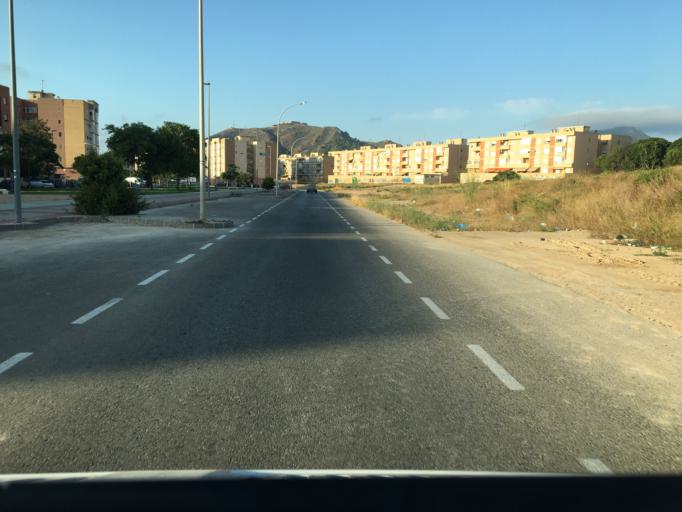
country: ES
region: Murcia
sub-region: Murcia
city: Cartagena
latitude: 37.6244
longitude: -1.0052
